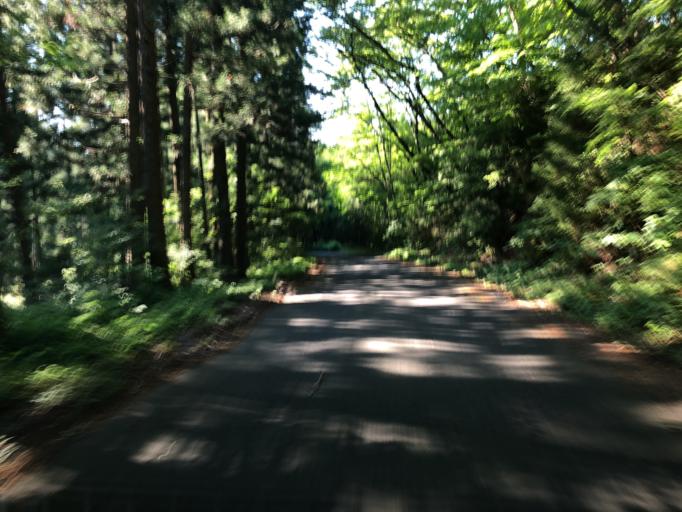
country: JP
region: Ibaraki
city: Kitaibaraki
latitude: 36.8743
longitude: 140.6688
